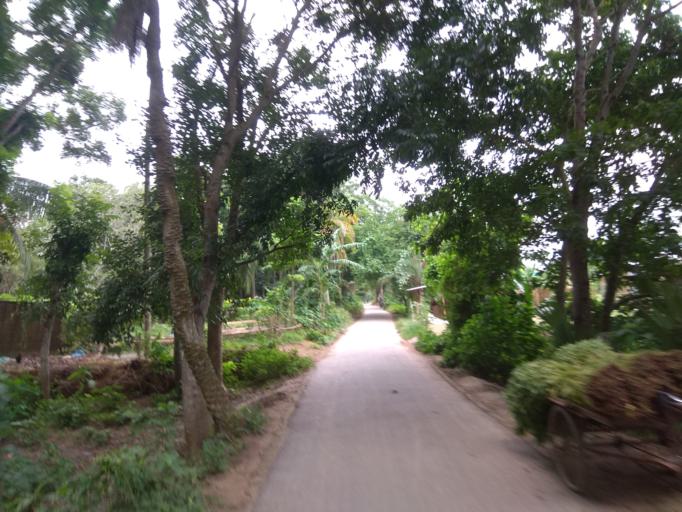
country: BD
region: Dhaka
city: Dohar
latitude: 23.4835
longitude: 90.0106
